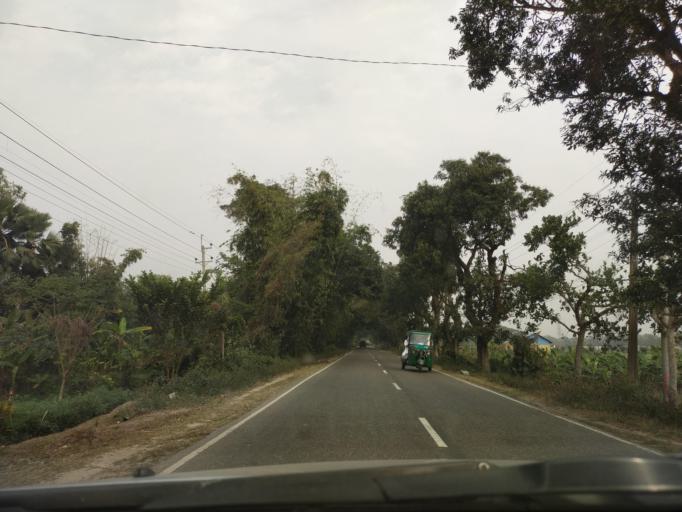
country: BD
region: Dhaka
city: Narsingdi
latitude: 24.0039
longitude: 90.7375
